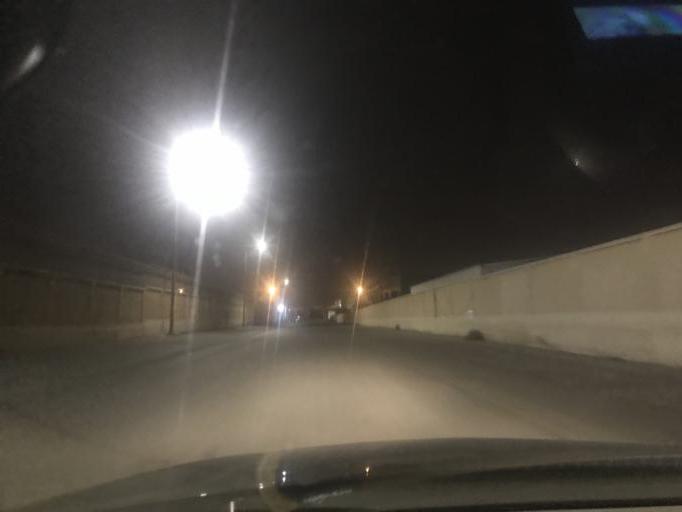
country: SA
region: Ar Riyad
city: Riyadh
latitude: 24.7237
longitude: 46.7838
